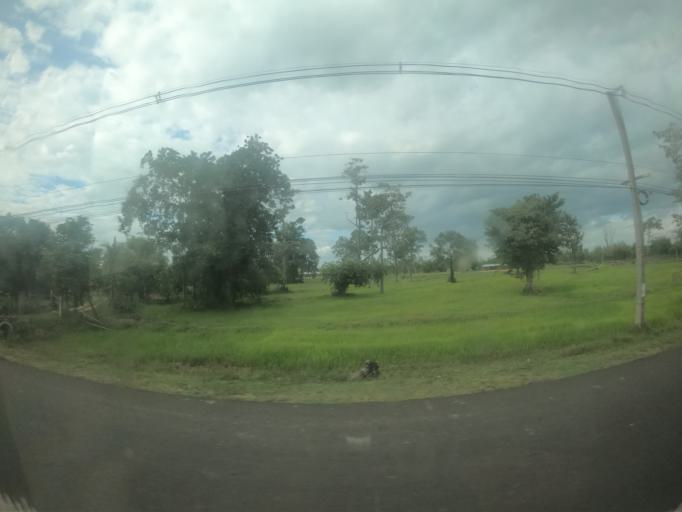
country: TH
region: Surin
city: Kap Choeng
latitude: 14.5566
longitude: 103.5032
